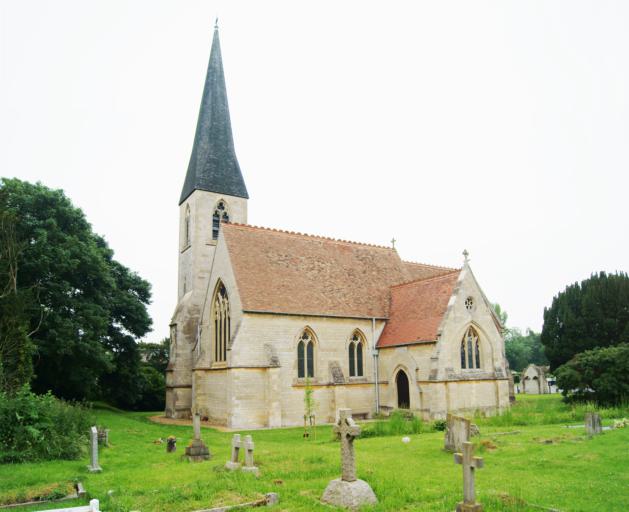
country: GB
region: England
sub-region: Cambridgeshire
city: Gamlingay
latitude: 52.1749
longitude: -0.1746
